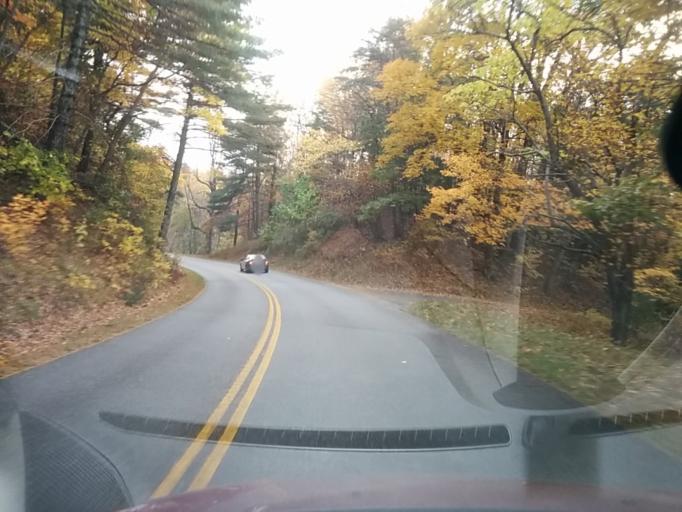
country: US
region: Virginia
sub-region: City of Buena Vista
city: Buena Vista
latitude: 37.8055
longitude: -79.2475
